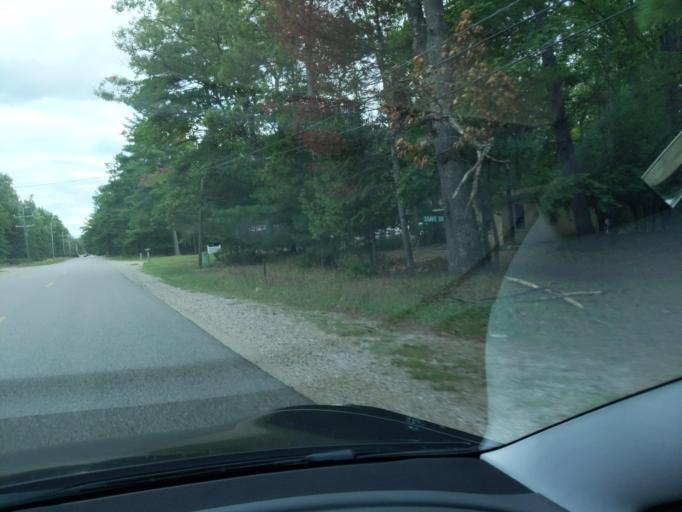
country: US
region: Michigan
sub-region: Kalkaska County
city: Rapid City
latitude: 44.8496
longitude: -85.3124
